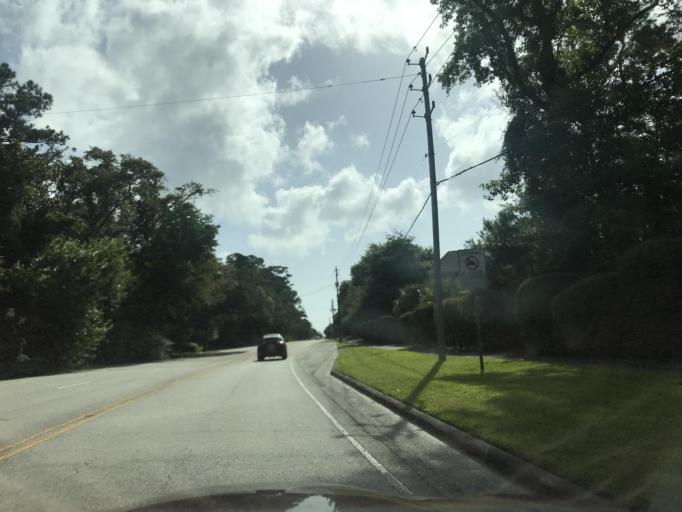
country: US
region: North Carolina
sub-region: New Hanover County
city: Seagate
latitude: 34.2205
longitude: -77.8301
